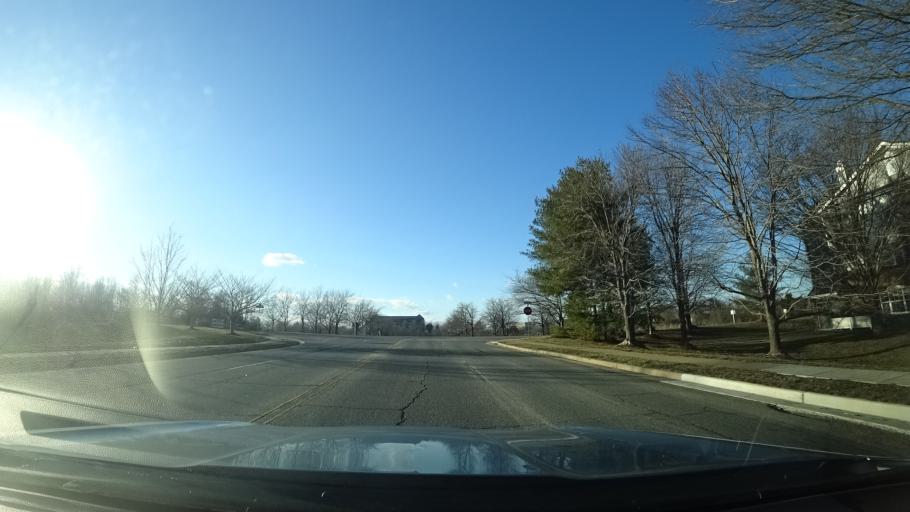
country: US
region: Virginia
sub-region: Loudoun County
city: University Center
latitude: 39.0531
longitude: -77.4403
